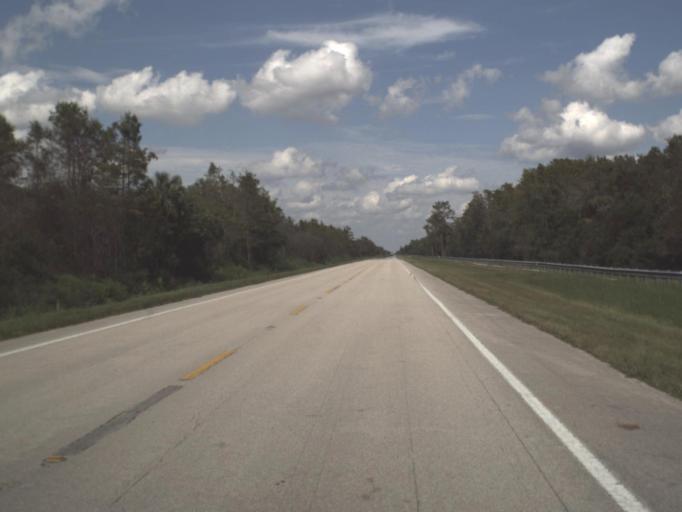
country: US
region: Florida
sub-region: Collier County
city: Orangetree
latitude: 26.0794
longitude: -81.3446
